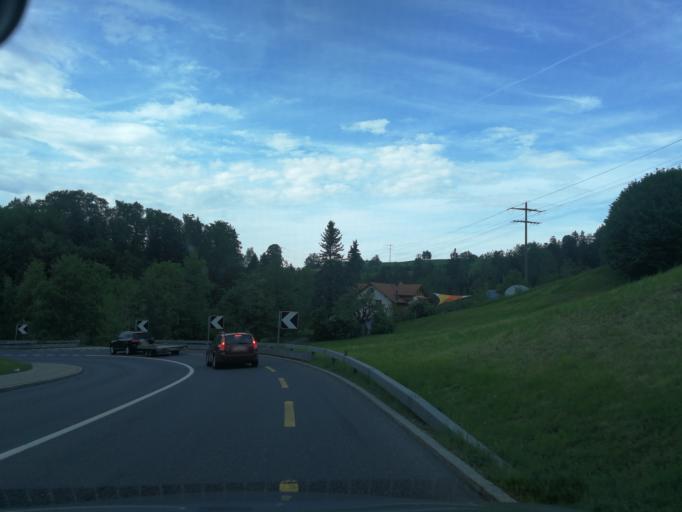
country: CH
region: Lucerne
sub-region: Entlebuch District
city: Wolhusen
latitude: 47.0350
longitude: 8.0734
